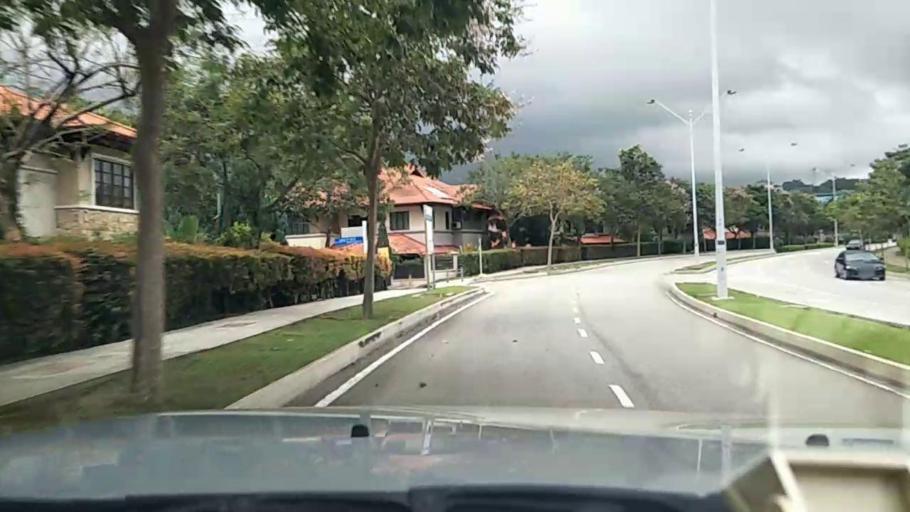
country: MY
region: Putrajaya
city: Putrajaya
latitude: 2.9327
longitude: 101.7041
